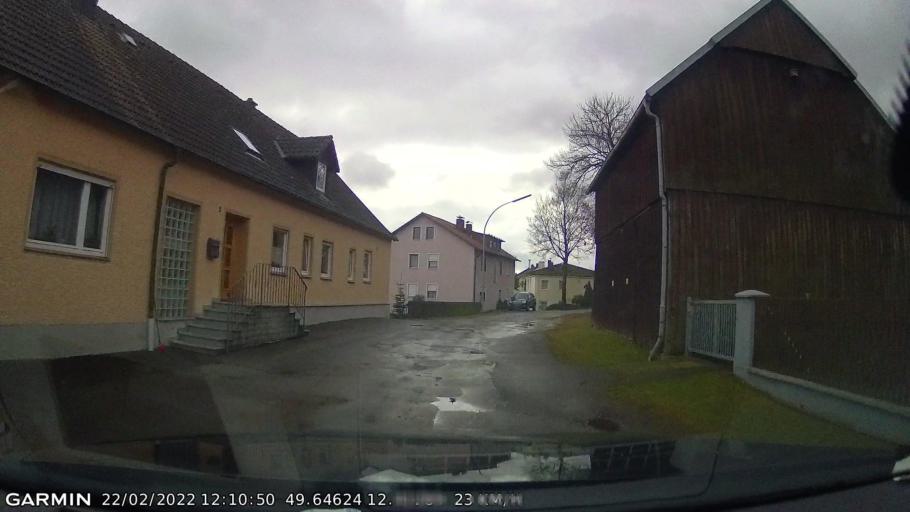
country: DE
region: Bavaria
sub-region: Upper Palatinate
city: Pleystein
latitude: 49.6462
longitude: 12.4129
